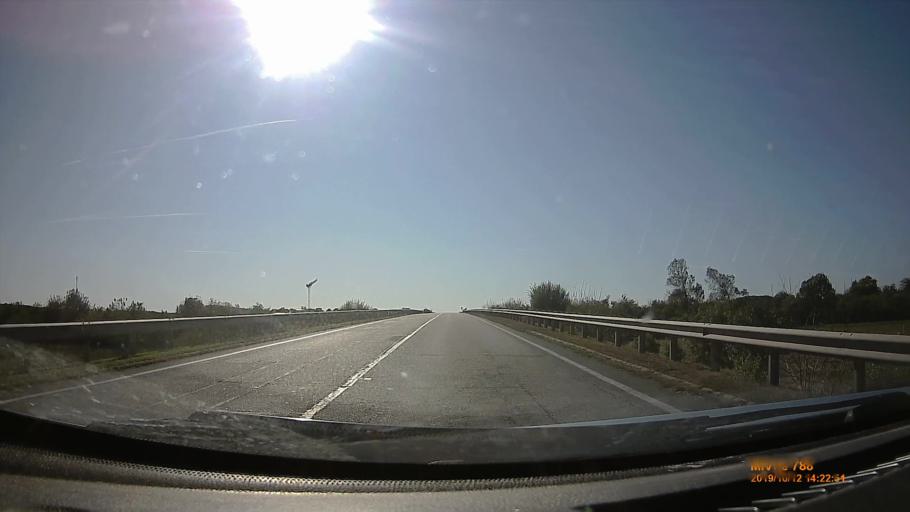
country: HU
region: Hajdu-Bihar
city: Biharkeresztes
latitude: 47.1402
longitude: 21.7092
